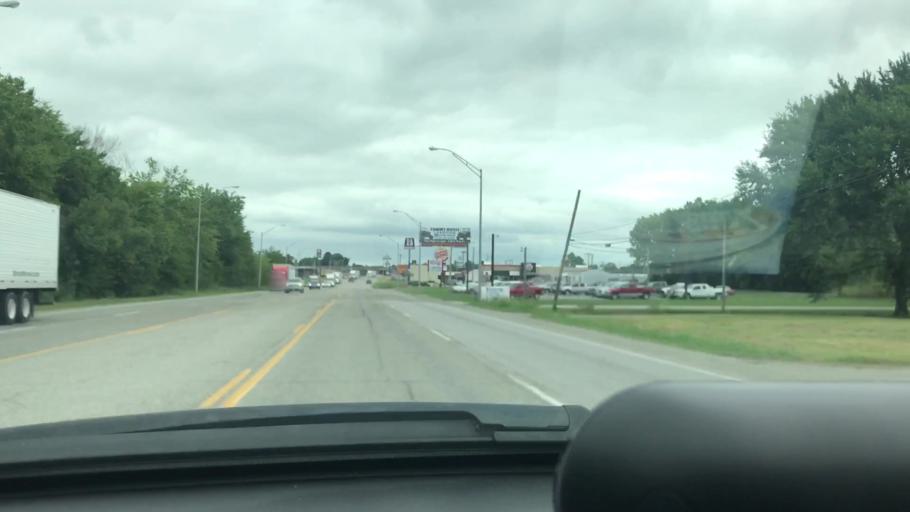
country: US
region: Oklahoma
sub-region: Wagoner County
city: Wagoner
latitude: 35.9539
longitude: -95.3952
